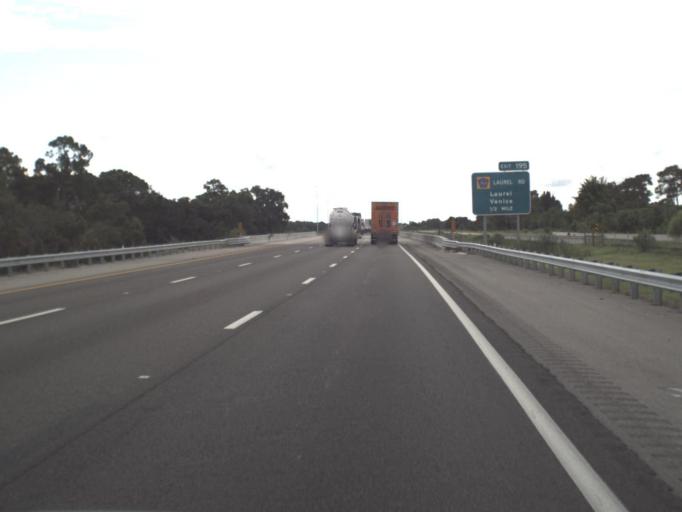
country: US
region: Florida
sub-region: Sarasota County
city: Nokomis
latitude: 27.1489
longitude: -82.4191
